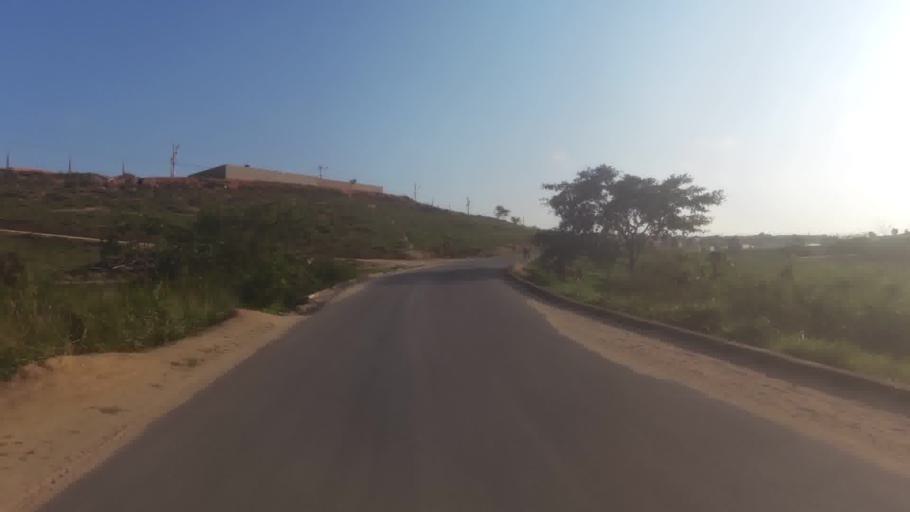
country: BR
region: Espirito Santo
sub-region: Itapemirim
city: Itapemirim
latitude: -21.0171
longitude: -40.8302
